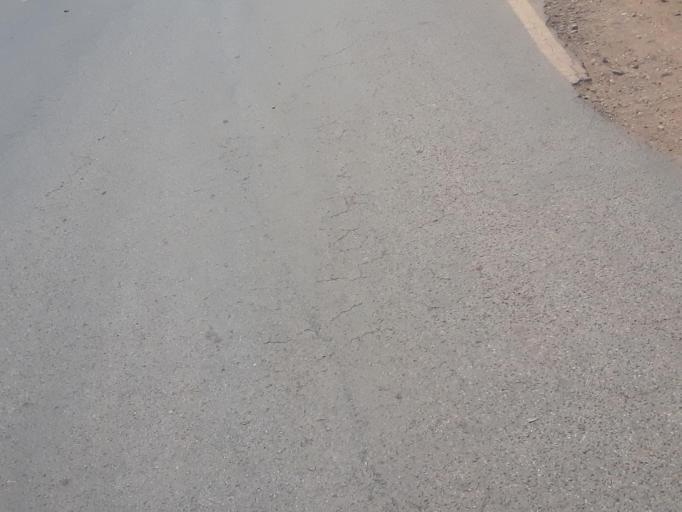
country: ZM
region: Lusaka
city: Lusaka
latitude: -15.3590
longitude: 28.2791
